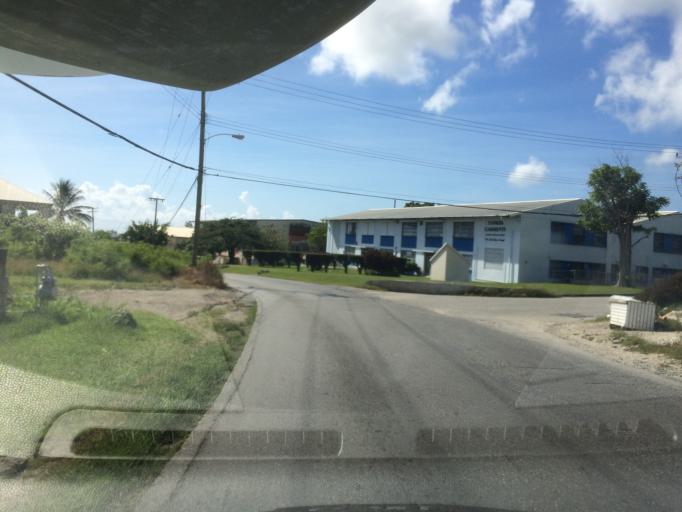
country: BB
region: Christ Church
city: Oistins
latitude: 13.0788
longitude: -59.5334
